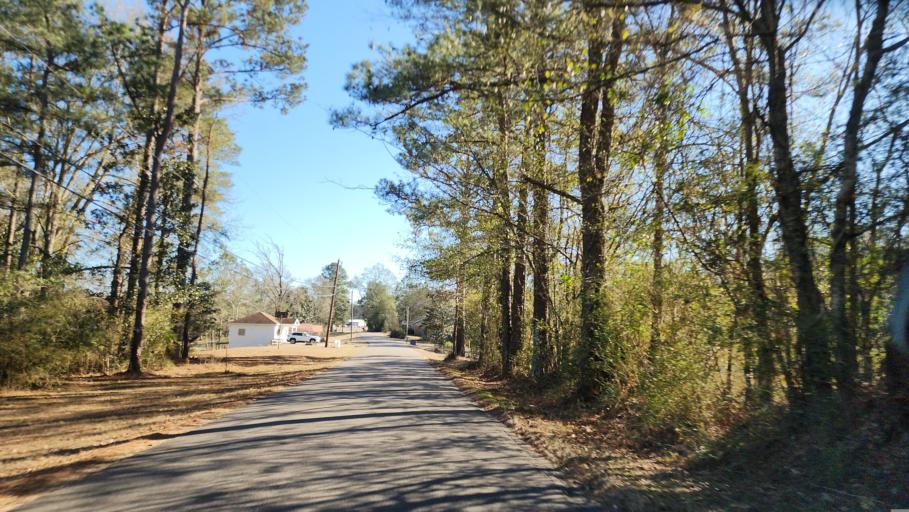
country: US
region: Mississippi
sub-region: Jones County
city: Laurel
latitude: 31.7054
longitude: -89.0923
